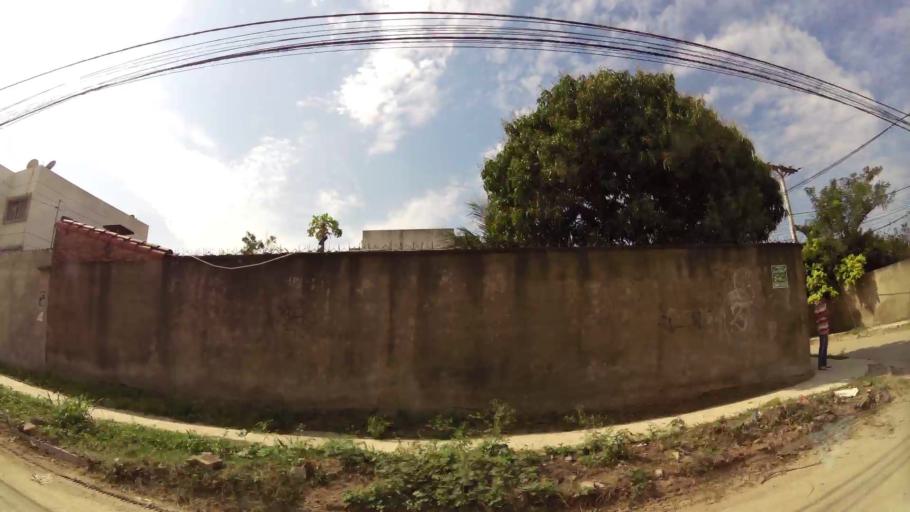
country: BO
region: Santa Cruz
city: Santa Cruz de la Sierra
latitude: -17.7204
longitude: -63.1742
